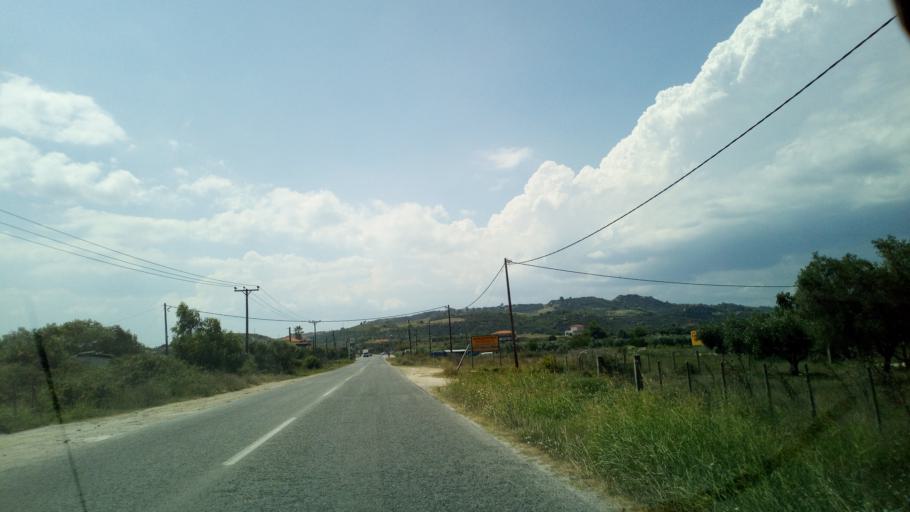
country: GR
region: Central Macedonia
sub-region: Nomos Chalkidikis
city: Agios Nikolaos
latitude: 40.2331
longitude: 23.7210
